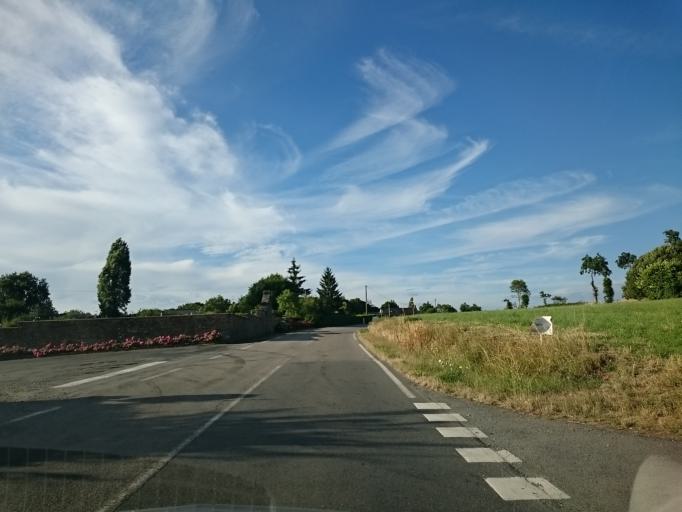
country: FR
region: Brittany
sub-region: Departement d'Ille-et-Vilaine
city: Pance
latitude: 47.8988
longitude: -1.6076
